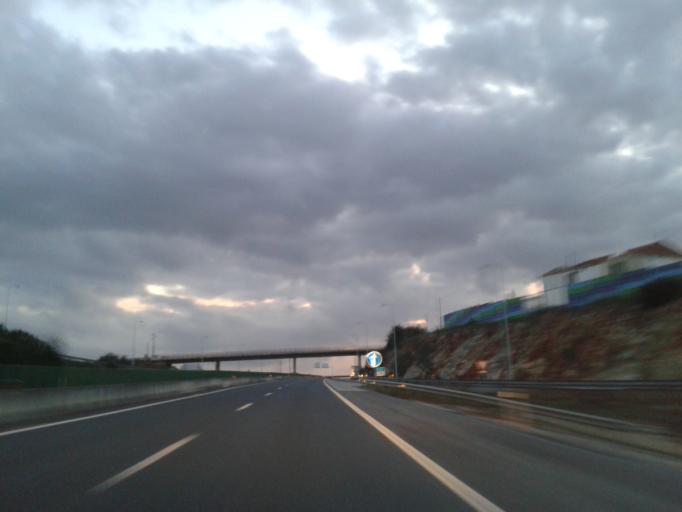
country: PT
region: Faro
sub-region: Albufeira
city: Ferreiras
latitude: 37.1531
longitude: -8.2113
